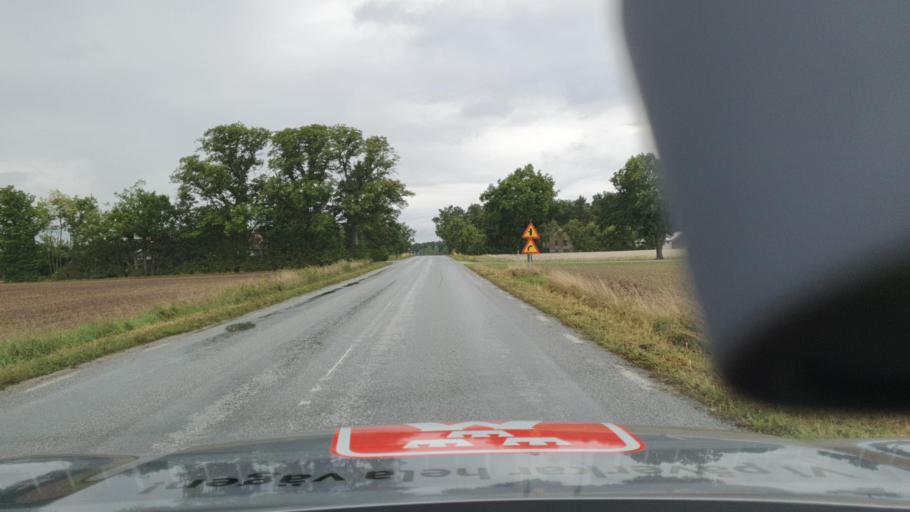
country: SE
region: Gotland
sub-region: Gotland
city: Visby
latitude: 57.5035
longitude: 18.4352
